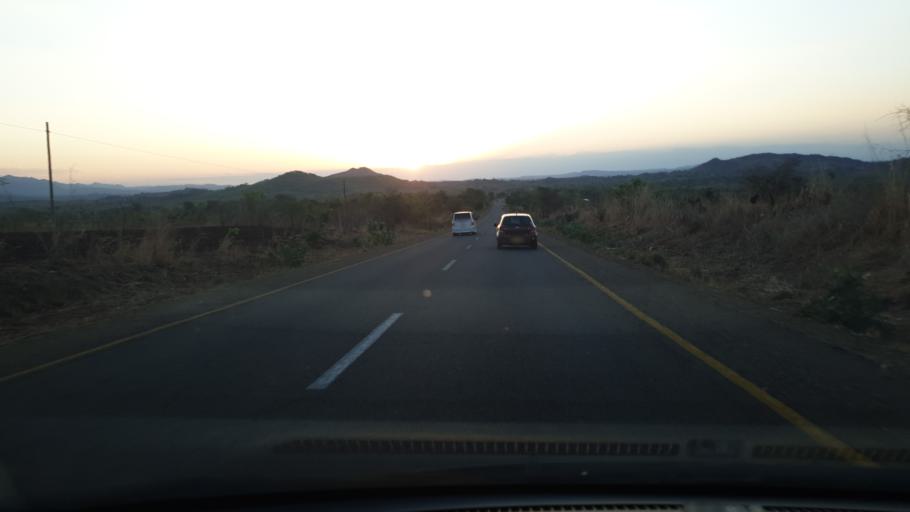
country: MW
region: Central Region
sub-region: Salima District
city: Salima
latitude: -13.7496
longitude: 34.3052
